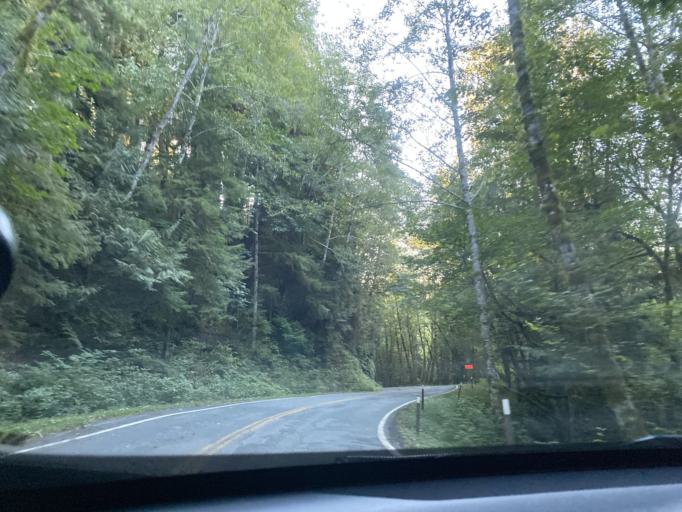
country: US
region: Washington
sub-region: Clallam County
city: Forks
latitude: 47.8233
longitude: -124.2026
